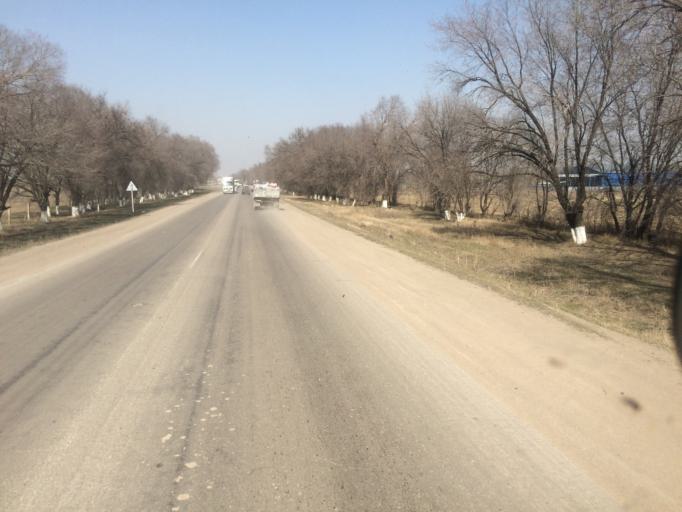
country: KZ
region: Almaty Oblysy
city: Burunday
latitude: 43.3278
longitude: 76.6623
